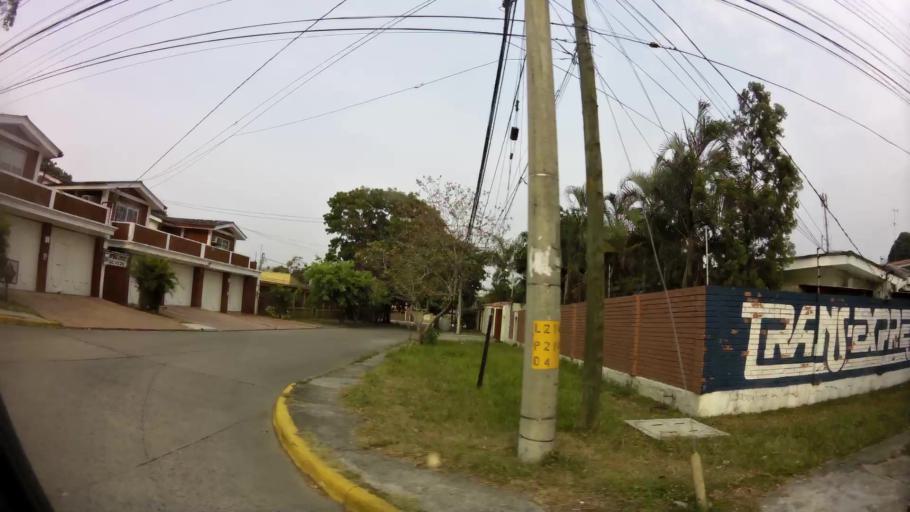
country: HN
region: Cortes
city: San Pedro Sula
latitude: 15.5128
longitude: -88.0313
